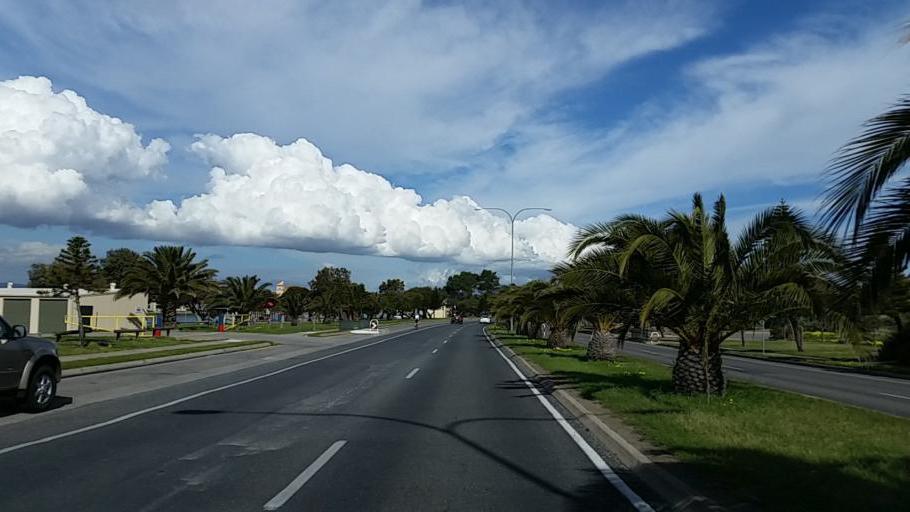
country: AU
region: South Australia
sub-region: Charles Sturt
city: West Lakes Shore
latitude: -34.8751
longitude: 138.4840
